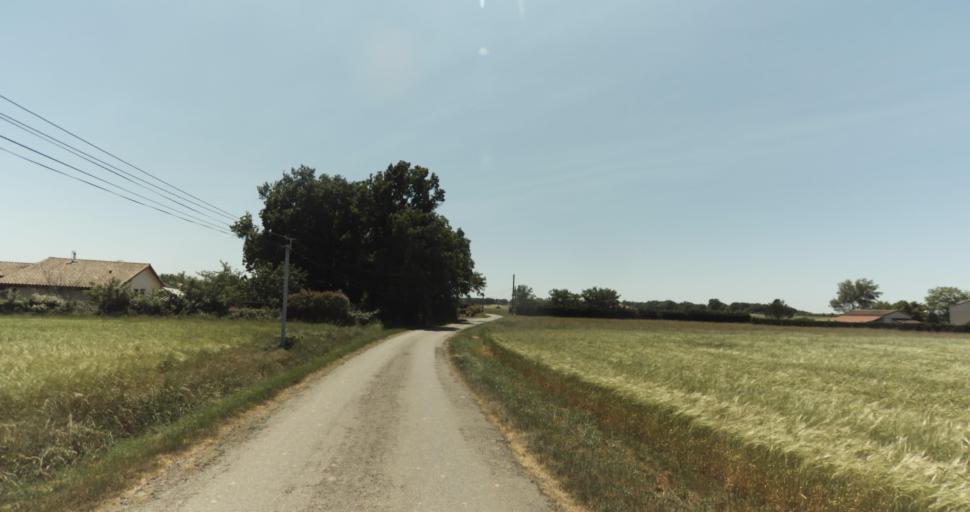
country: FR
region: Midi-Pyrenees
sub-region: Departement de la Haute-Garonne
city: Levignac
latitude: 43.6392
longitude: 1.1893
